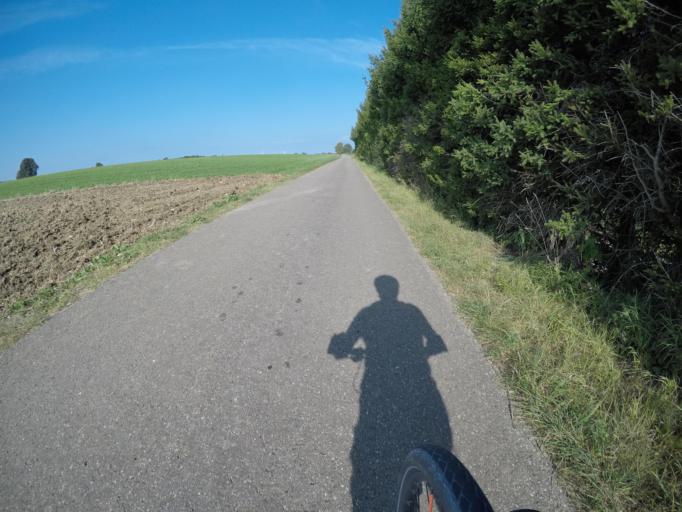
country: DE
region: Baden-Wuerttemberg
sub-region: Regierungsbezirk Stuttgart
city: Gerstetten
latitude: 48.6336
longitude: 9.9768
